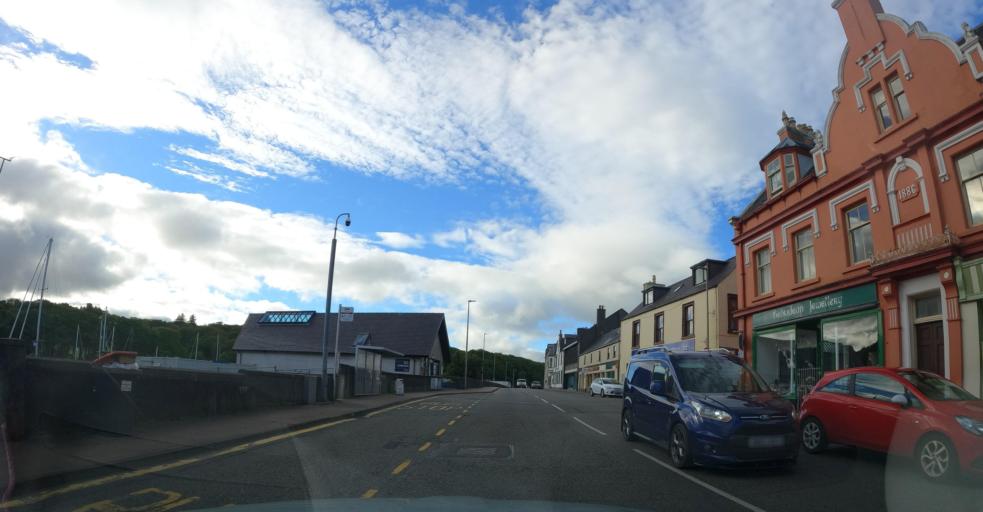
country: GB
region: Scotland
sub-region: Eilean Siar
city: Stornoway
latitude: 58.2097
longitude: -6.3887
